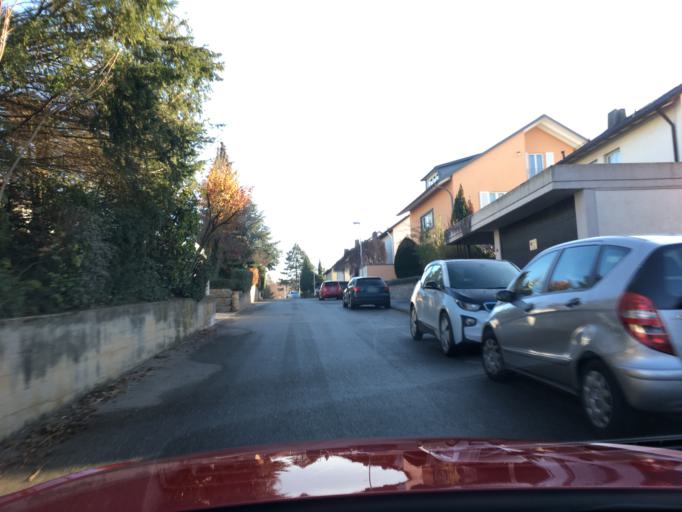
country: DE
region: Baden-Wuerttemberg
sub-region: Regierungsbezirk Stuttgart
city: Heilbronn
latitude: 49.1325
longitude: 9.2344
